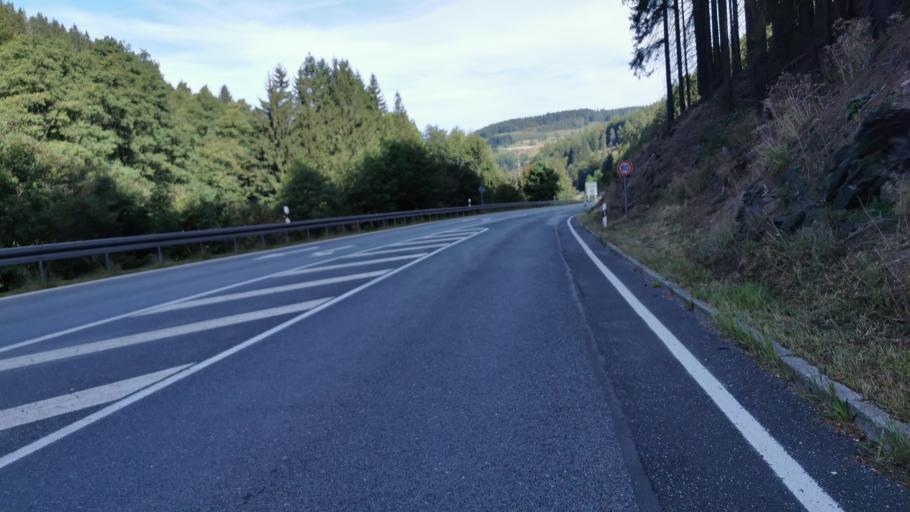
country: DE
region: Bavaria
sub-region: Upper Franconia
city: Ludwigsstadt
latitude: 50.4732
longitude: 11.3942
